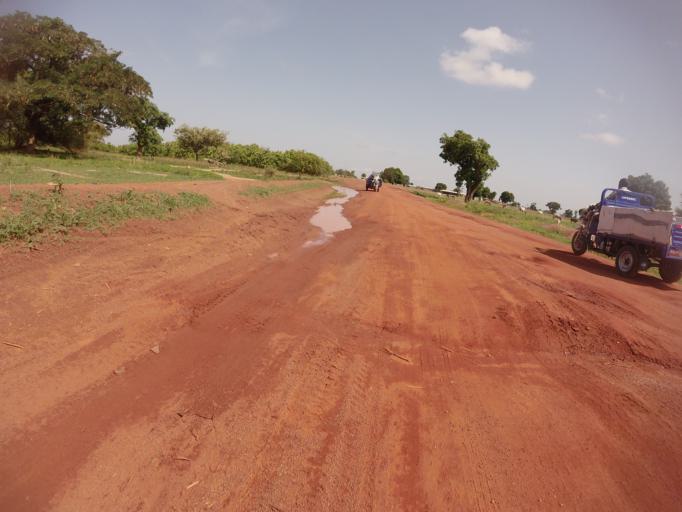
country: GH
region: Upper East
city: Bawku
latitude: 11.0097
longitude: -0.2011
